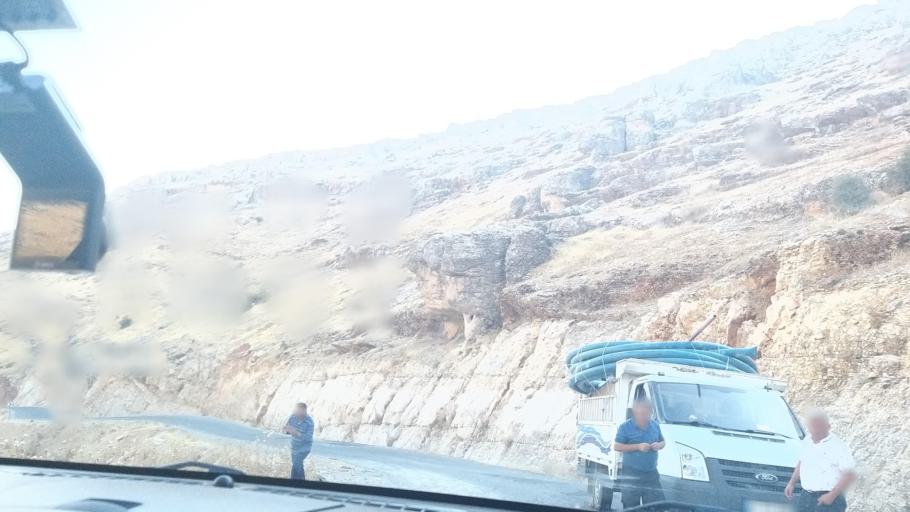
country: TR
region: Diyarbakir
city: Silvan
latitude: 38.1651
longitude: 41.0013
